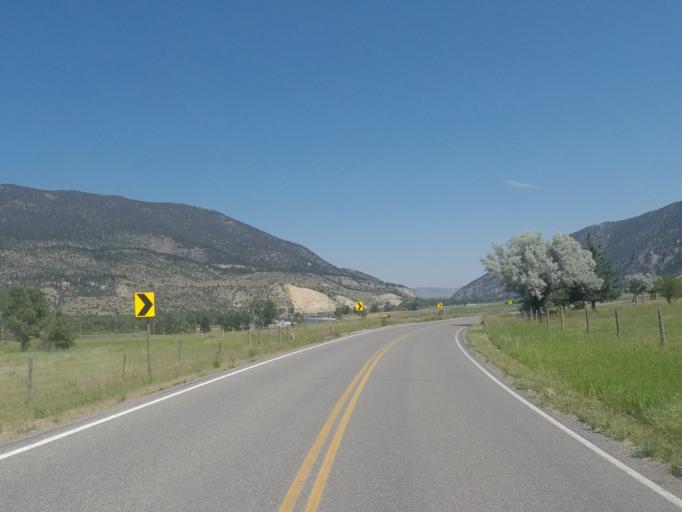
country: US
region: Montana
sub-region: Park County
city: Livingston
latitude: 45.5729
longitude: -110.5668
